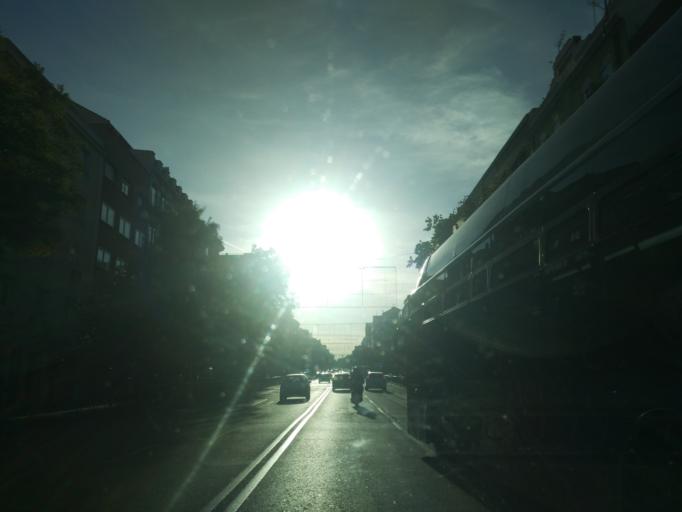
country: ES
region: Madrid
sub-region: Provincia de Madrid
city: Carabanchel
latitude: 40.3956
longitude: -3.7197
